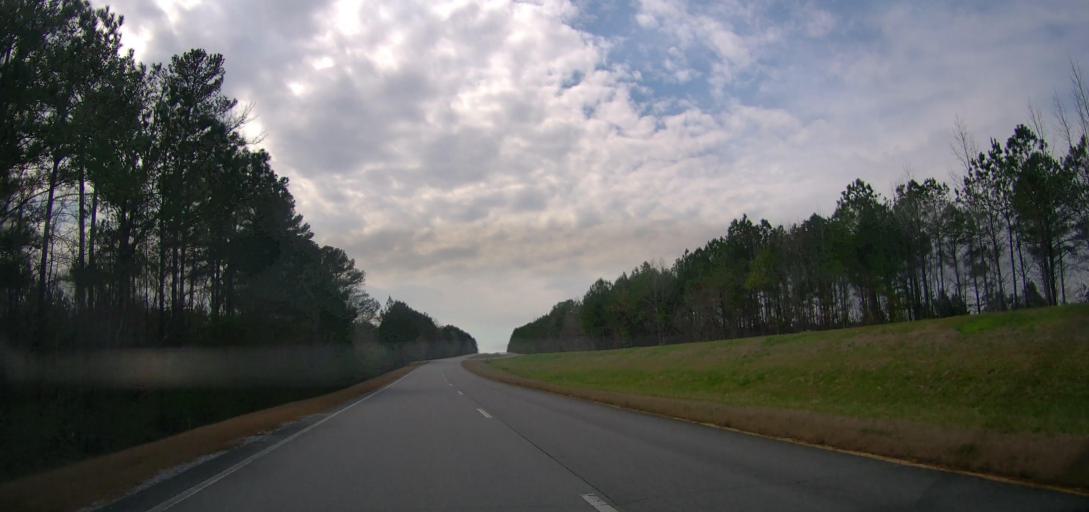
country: US
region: Alabama
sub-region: Marion County
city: Winfield
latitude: 33.9304
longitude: -87.6891
